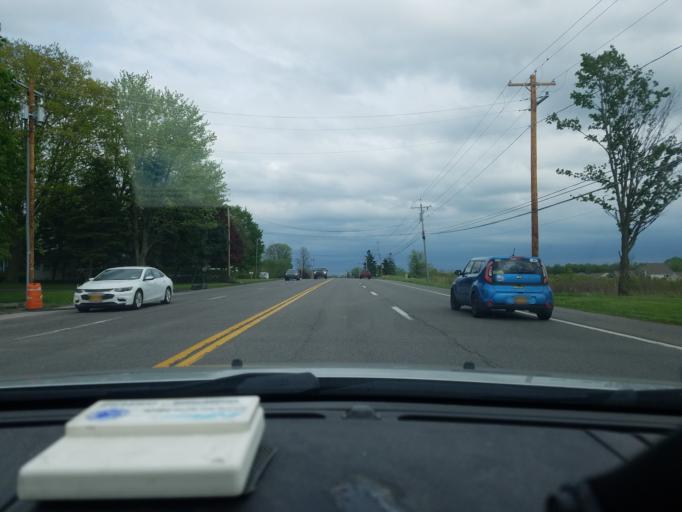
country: US
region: New York
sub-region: Onondaga County
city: Galeville
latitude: 43.1211
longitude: -76.1743
